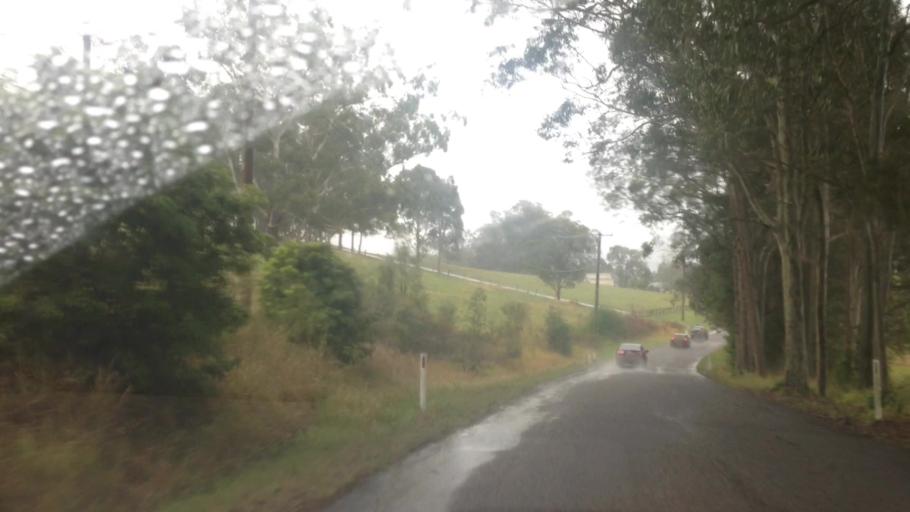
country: AU
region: New South Wales
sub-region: Wyong Shire
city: Little Jilliby
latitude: -33.1998
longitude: 151.3624
